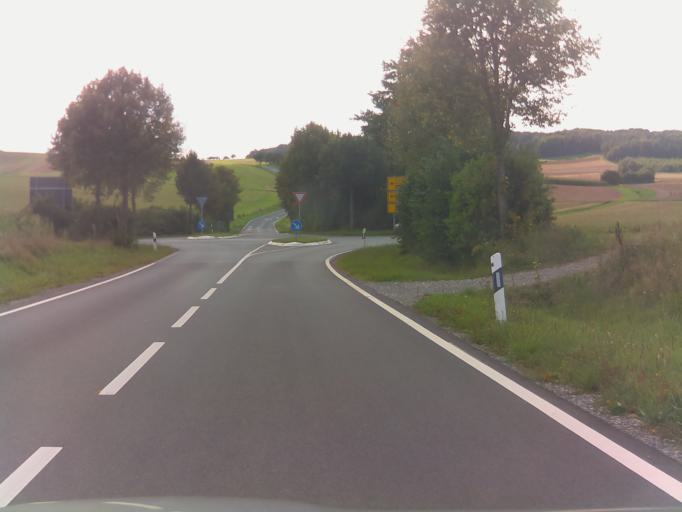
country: DE
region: Bavaria
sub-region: Regierungsbezirk Unterfranken
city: Neubrunn
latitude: 49.7229
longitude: 9.6351
